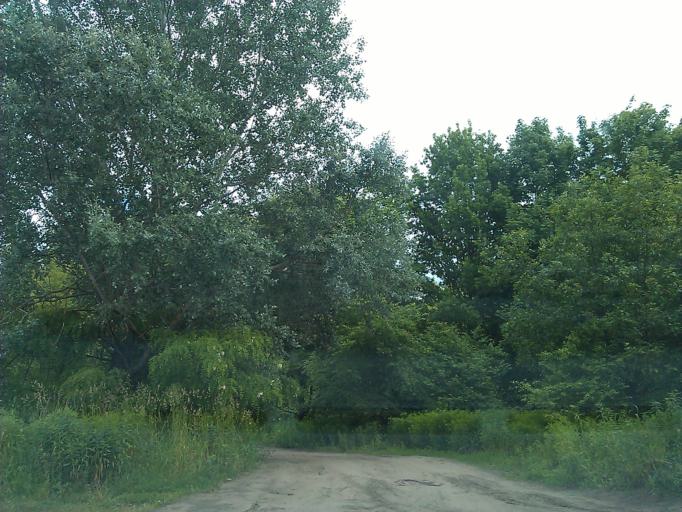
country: LV
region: Riga
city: Jaunciems
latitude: 56.9924
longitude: 24.2033
